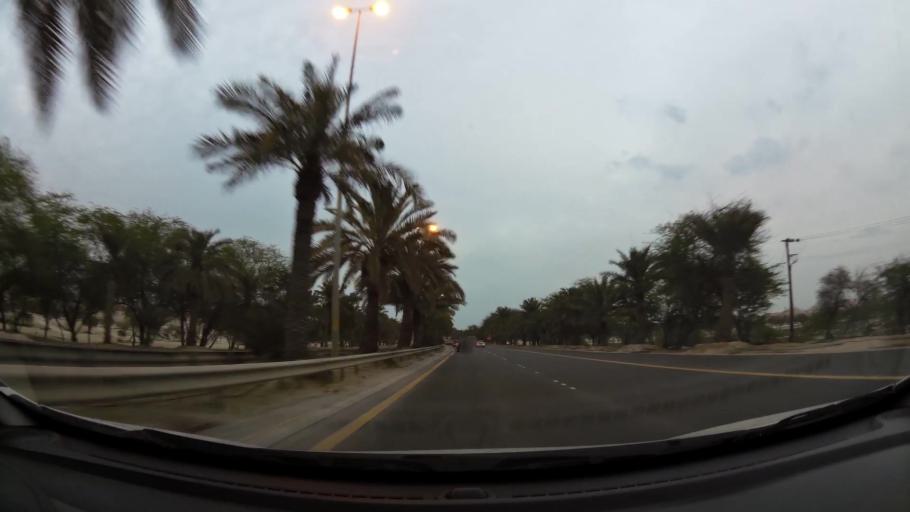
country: BH
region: Northern
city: Ar Rifa'
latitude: 26.1072
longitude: 50.5714
